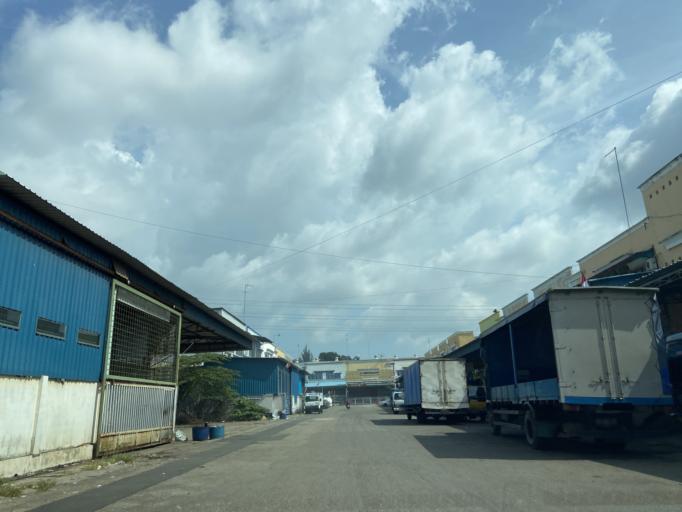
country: SG
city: Singapore
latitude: 1.1347
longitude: 104.0297
